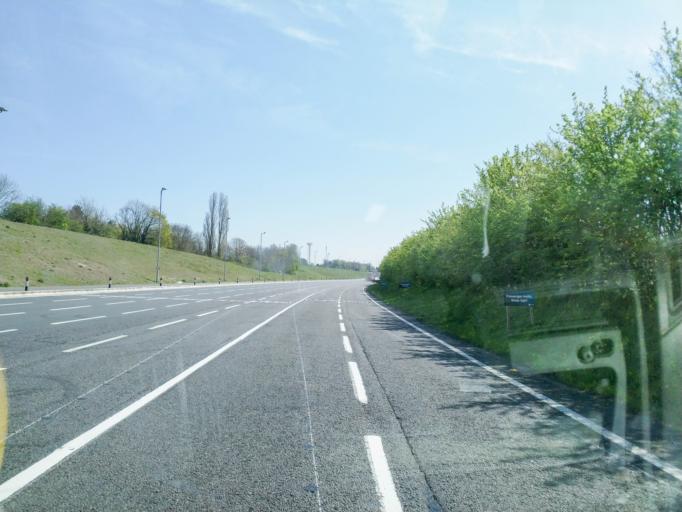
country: GB
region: England
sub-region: Kent
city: Hythe
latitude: 51.0940
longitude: 1.1055
